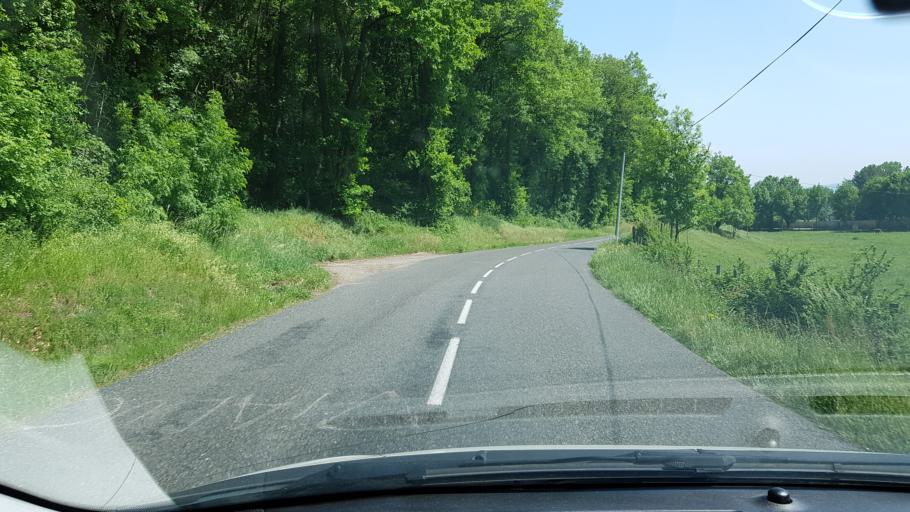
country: FR
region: Rhone-Alpes
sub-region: Departement du Rhone
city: Brignais
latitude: 45.6556
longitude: 4.7426
